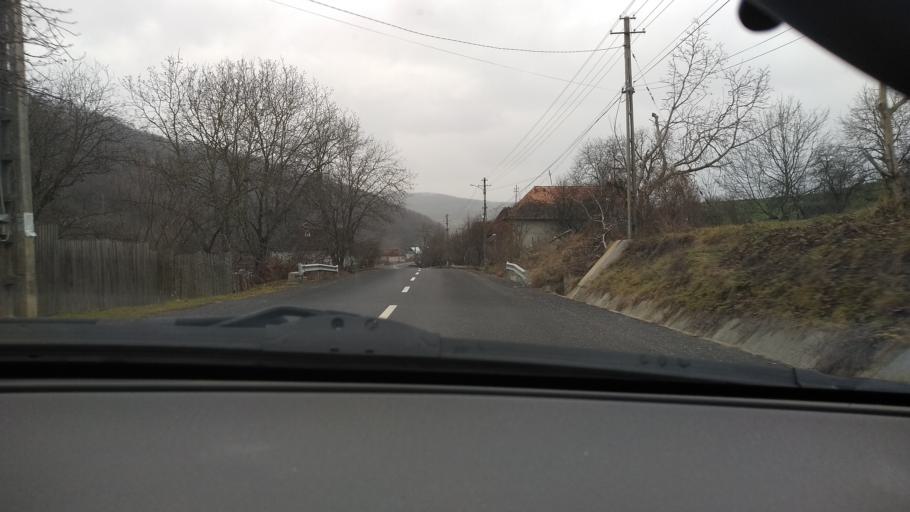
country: RO
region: Mures
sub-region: Comuna Magherani
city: Magherani
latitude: 46.5714
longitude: 24.9229
